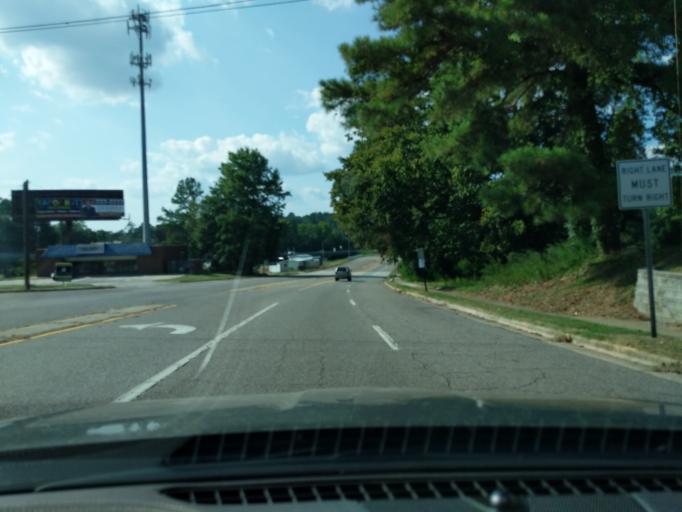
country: US
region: Georgia
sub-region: Richmond County
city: Augusta
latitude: 33.4903
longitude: -82.0078
